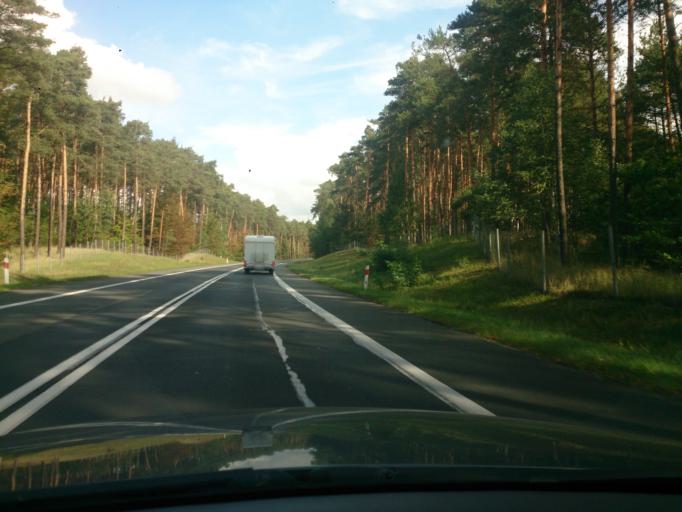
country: PL
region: Kujawsko-Pomorskie
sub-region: Powiat chelminski
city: Chelmno
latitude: 53.3983
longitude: 18.3511
